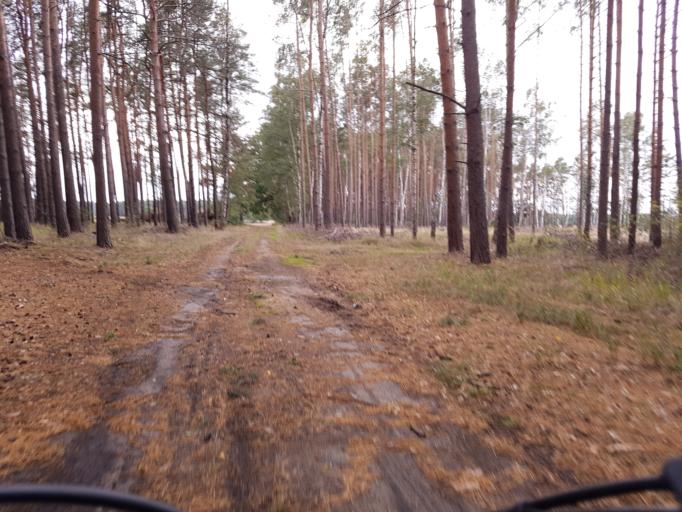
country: DE
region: Brandenburg
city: Schilda
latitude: 51.6097
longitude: 13.3759
